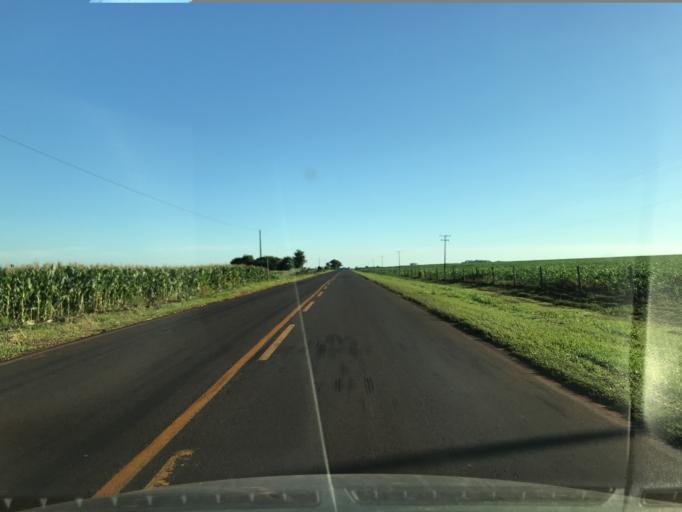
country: BR
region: Parana
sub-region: Palotina
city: Palotina
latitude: -24.1155
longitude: -53.8467
